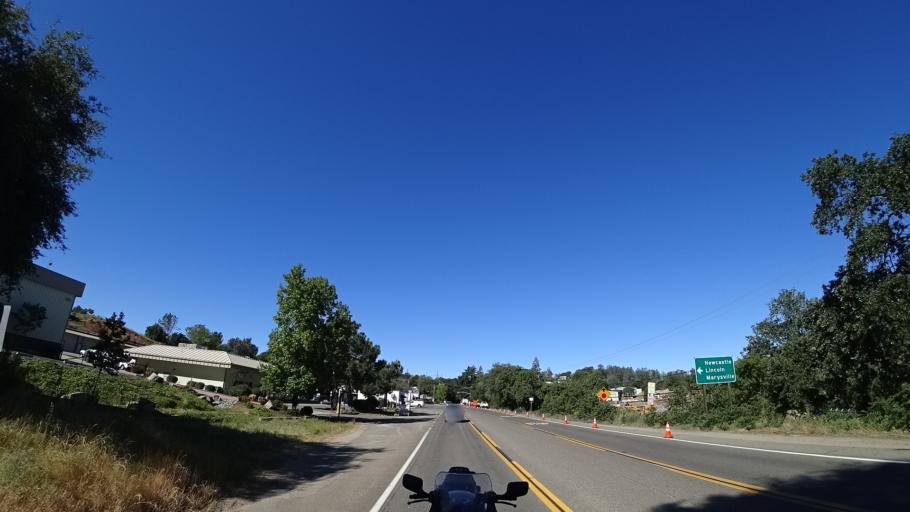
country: US
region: California
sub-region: Placer County
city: Newcastle
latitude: 38.8784
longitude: -121.1300
